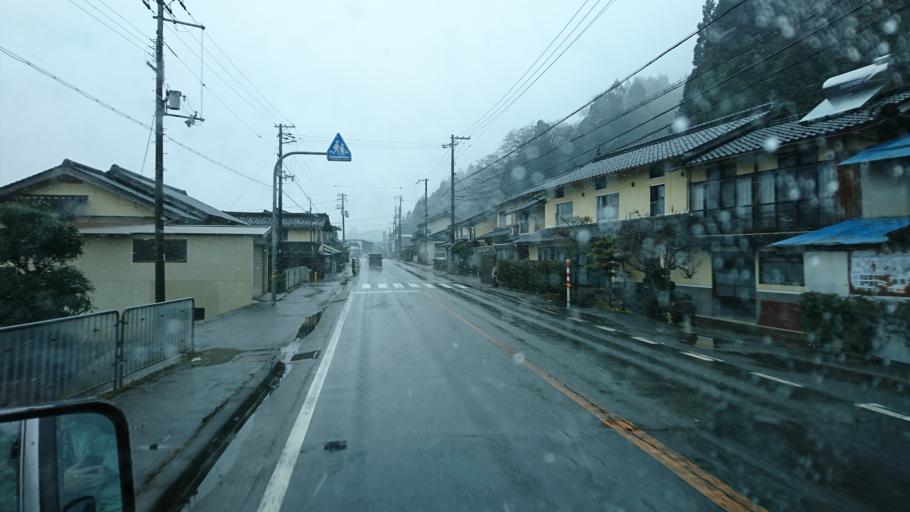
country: JP
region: Hyogo
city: Toyooka
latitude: 35.3797
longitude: 134.6497
